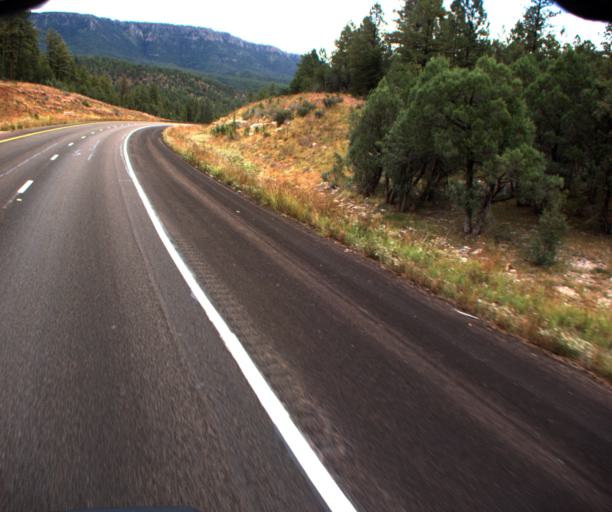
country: US
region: Arizona
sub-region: Gila County
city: Star Valley
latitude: 34.3261
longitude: -111.1036
